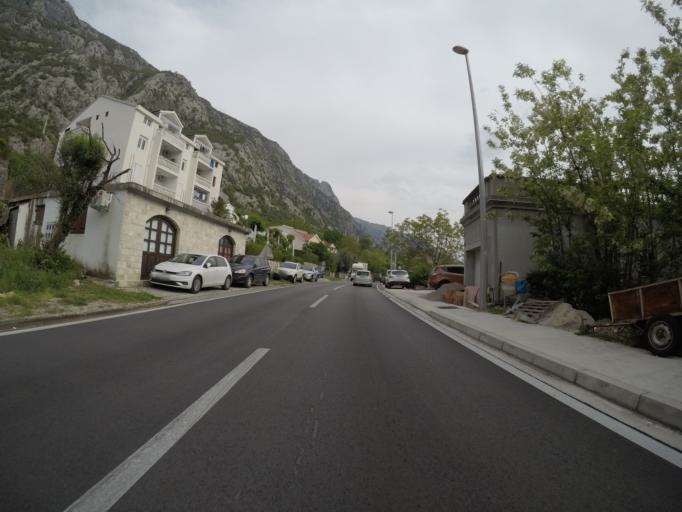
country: ME
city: Dobrota
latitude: 42.4594
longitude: 18.7657
